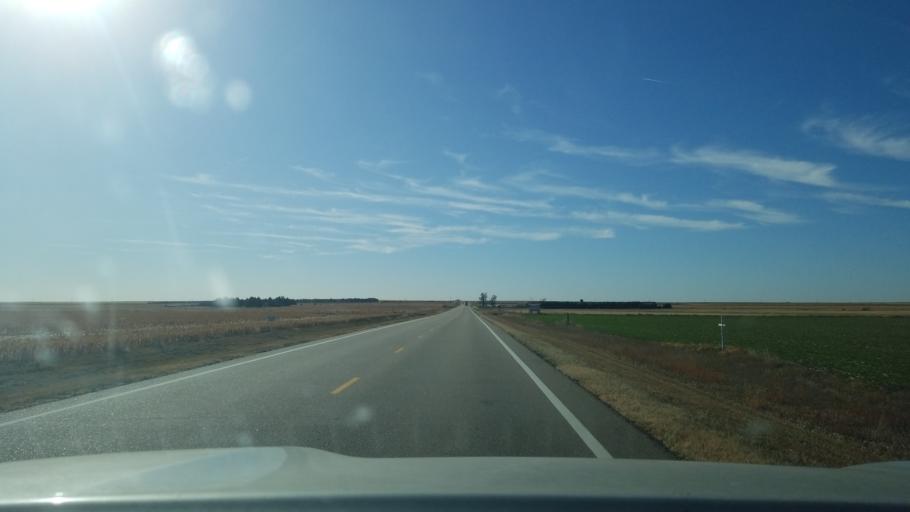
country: US
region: Kansas
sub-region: Ness County
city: Ness City
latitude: 38.3728
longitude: -99.8979
